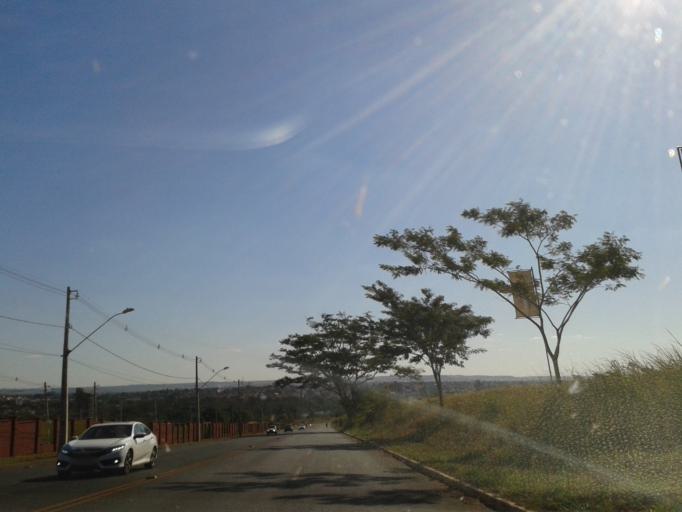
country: BR
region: Goias
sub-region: Itumbiara
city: Itumbiara
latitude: -18.4281
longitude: -49.1975
